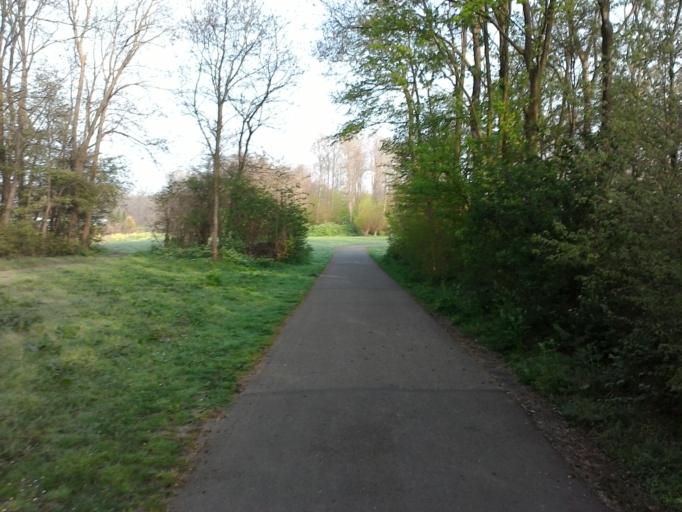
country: NL
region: Utrecht
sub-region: Stichtse Vecht
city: Maarssen
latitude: 52.1403
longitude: 5.0840
